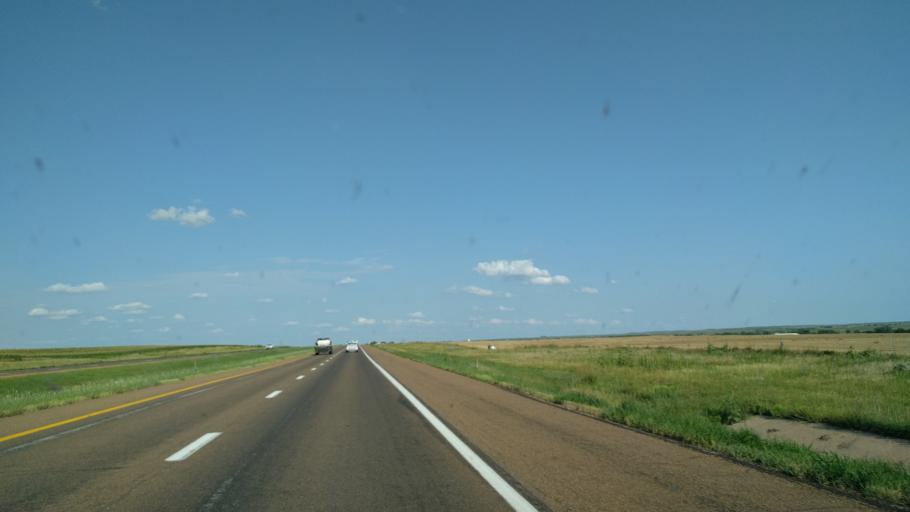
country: US
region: Kansas
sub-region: Ellis County
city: Ellis
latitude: 38.9484
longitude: -99.5201
